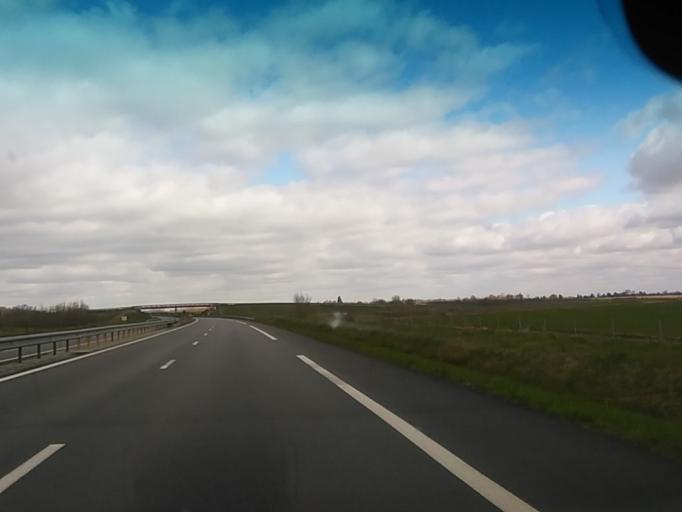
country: FR
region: Haute-Normandie
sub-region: Departement de l'Eure
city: Thiberville
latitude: 49.1176
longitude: 0.5264
